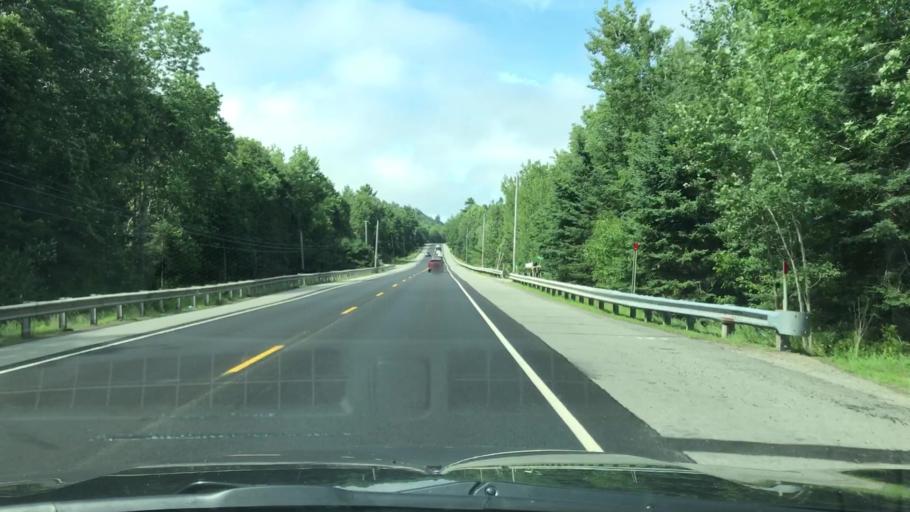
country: US
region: Maine
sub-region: Hancock County
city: Bucksport
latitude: 44.5361
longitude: -68.8089
